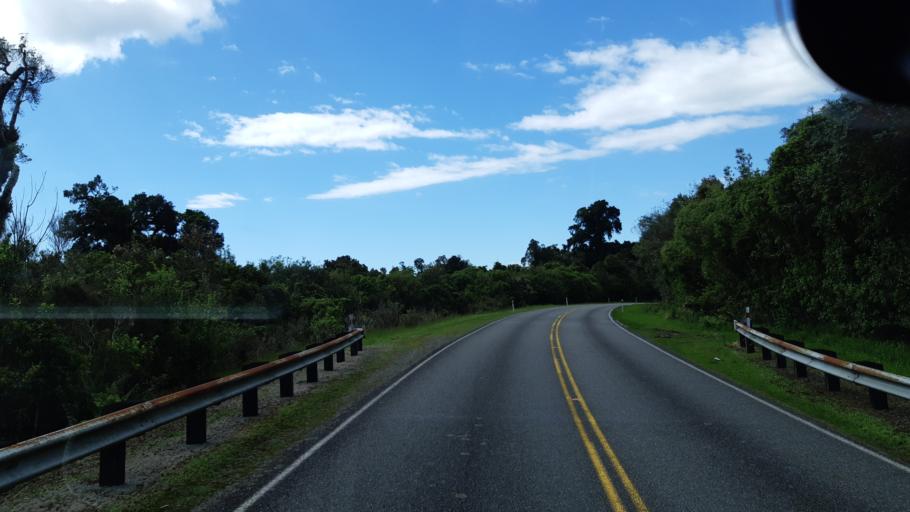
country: NZ
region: West Coast
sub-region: Westland District
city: Hokitika
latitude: -43.0693
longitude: 170.6274
